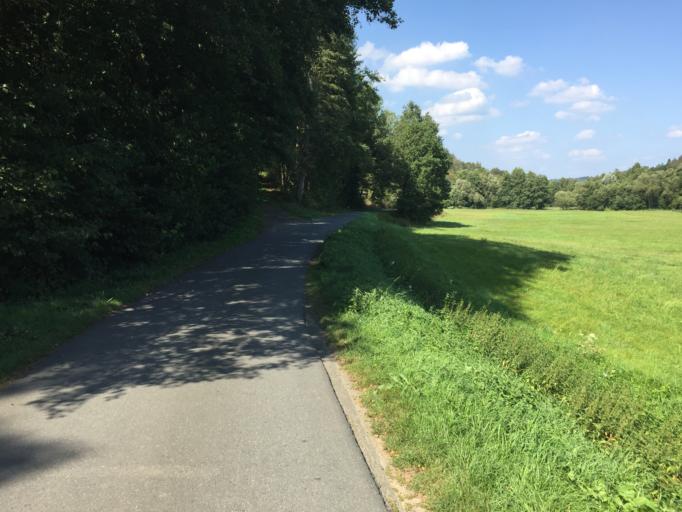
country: DE
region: Hesse
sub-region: Regierungsbezirk Giessen
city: Schwalbach
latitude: 50.4828
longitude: 8.4333
